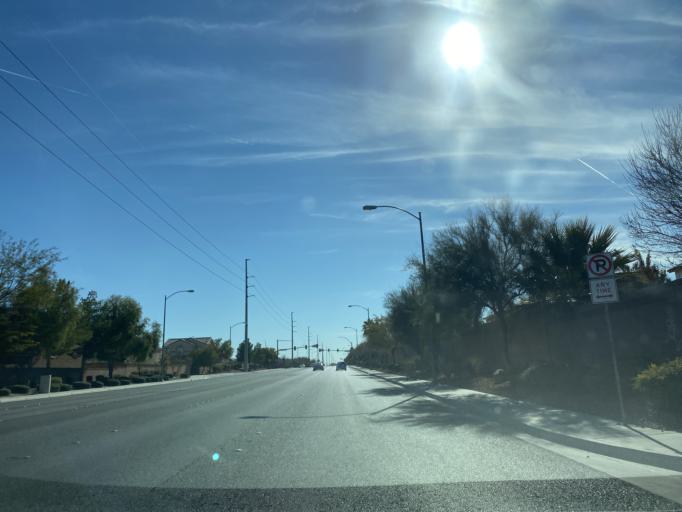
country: US
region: Nevada
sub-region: Clark County
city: North Las Vegas
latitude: 36.2338
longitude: -115.1435
